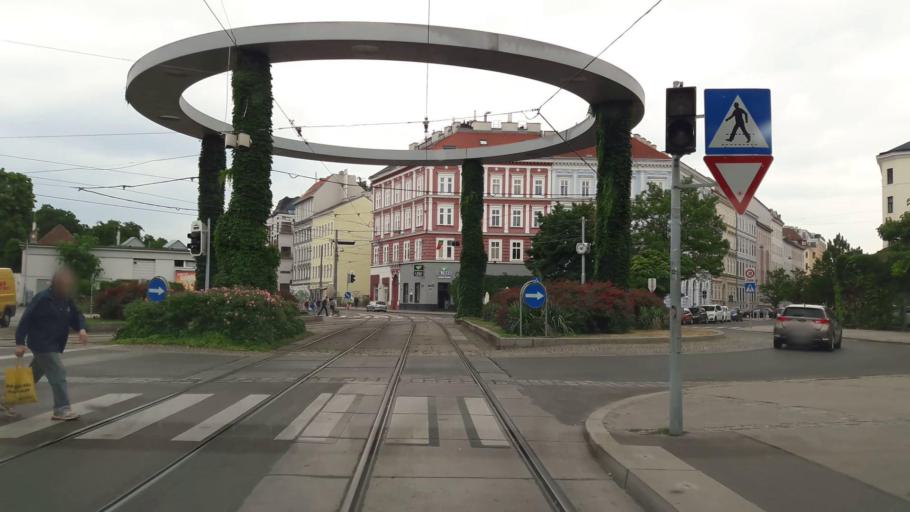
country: AT
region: Vienna
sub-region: Wien Stadt
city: Vienna
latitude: 48.2266
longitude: 16.3698
